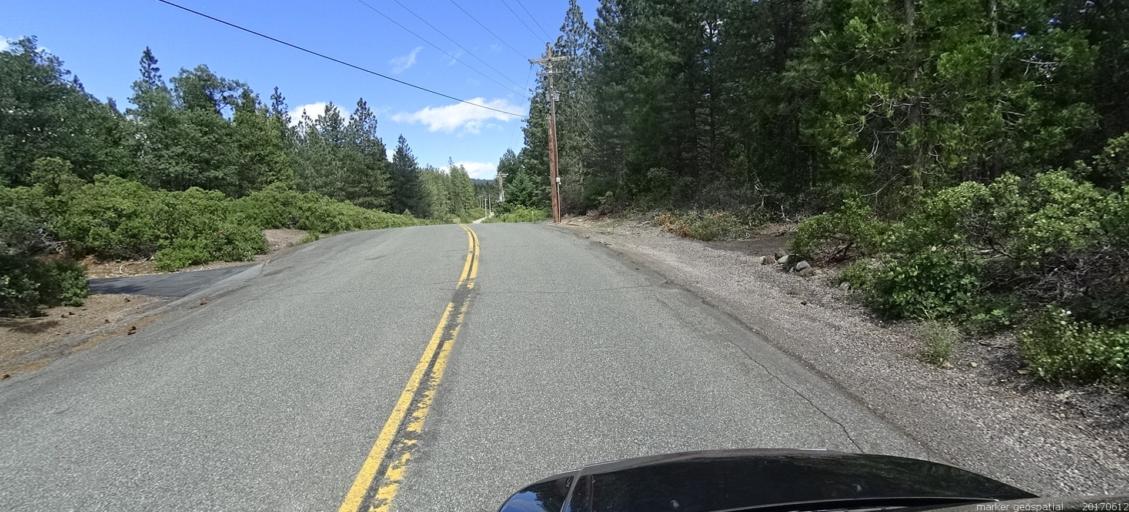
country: US
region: California
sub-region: Siskiyou County
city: Mount Shasta
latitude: 41.2987
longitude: -122.2886
